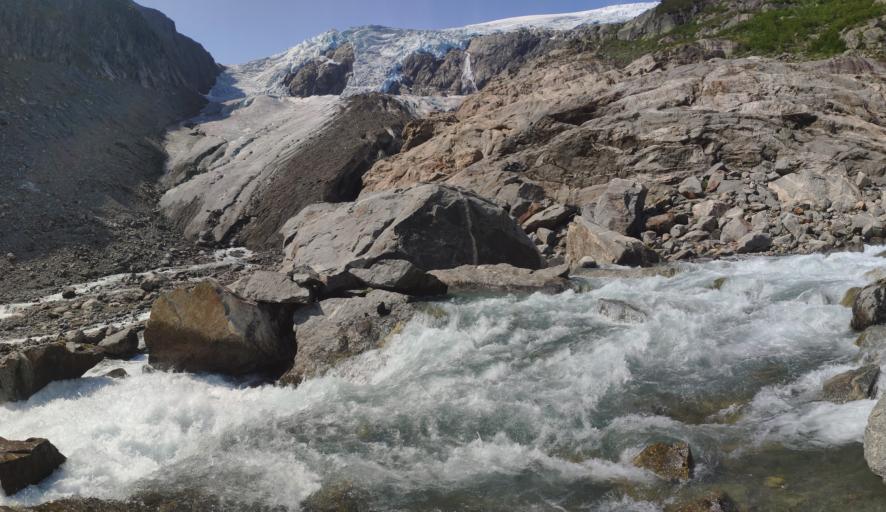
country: NO
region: Hordaland
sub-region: Odda
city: Odda
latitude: 60.0410
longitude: 6.4391
